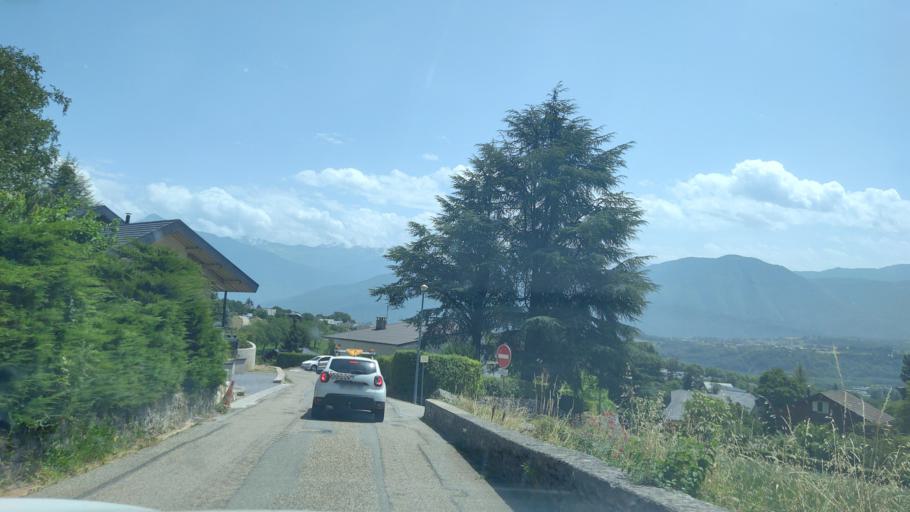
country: FR
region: Rhone-Alpes
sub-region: Departement de la Savoie
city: Coise-Saint-Jean-Pied-Gauthier
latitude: 45.5723
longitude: 6.1464
